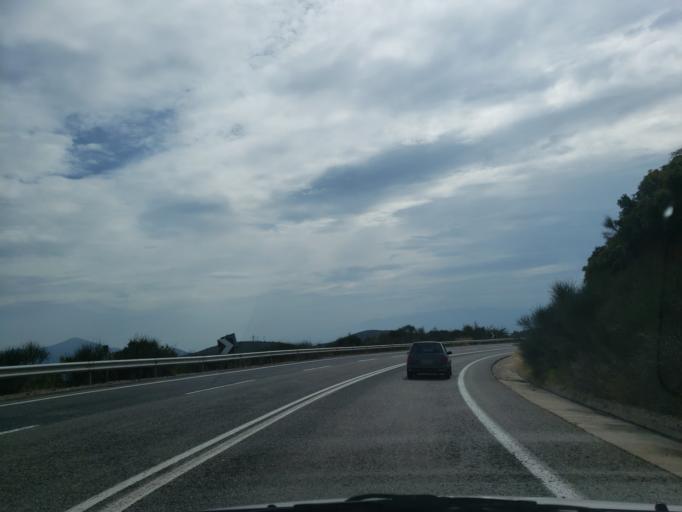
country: GR
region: Central Greece
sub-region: Nomos Fthiotidos
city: Stavros
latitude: 38.9771
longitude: 22.3819
